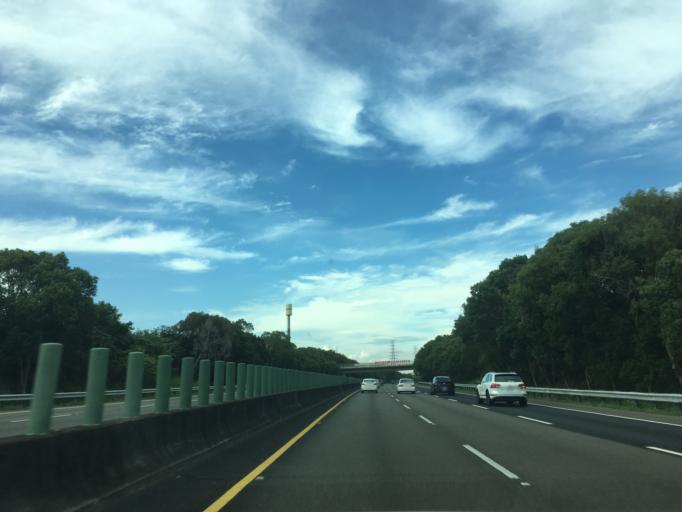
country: TW
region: Taiwan
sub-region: Chiayi
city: Jiayi Shi
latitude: 23.5793
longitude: 120.5093
